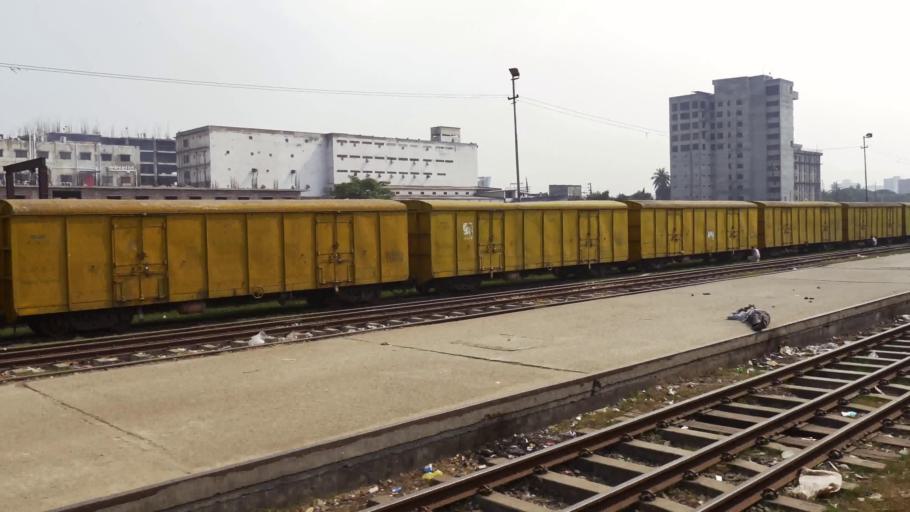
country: BD
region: Dhaka
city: Paltan
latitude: 23.7917
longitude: 90.4000
